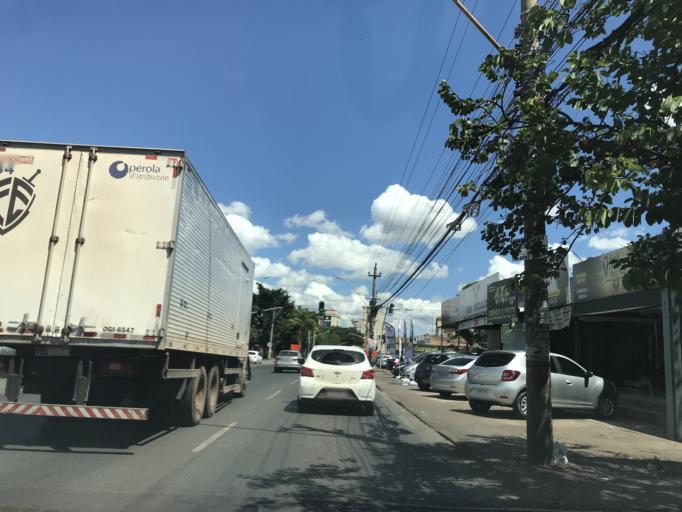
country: BR
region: Federal District
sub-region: Brasilia
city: Brasilia
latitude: -15.8376
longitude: -48.0590
